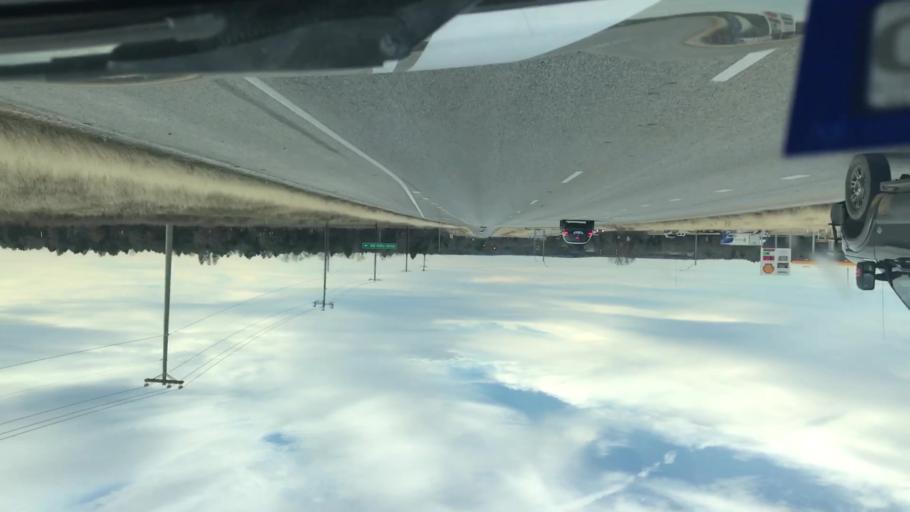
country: US
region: Texas
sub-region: Bastrop County
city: Elgin
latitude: 30.3120
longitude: -97.3071
